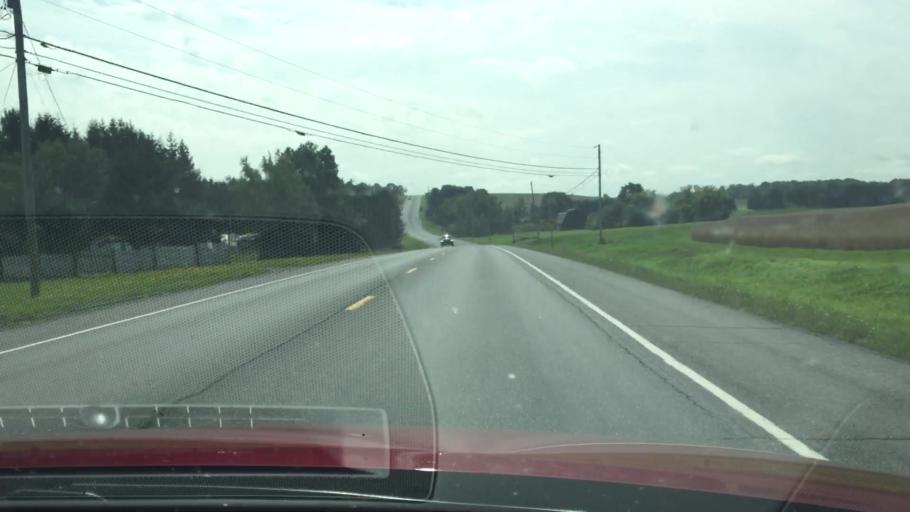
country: US
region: Maine
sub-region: Aroostook County
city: Easton
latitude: 46.5865
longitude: -67.9608
